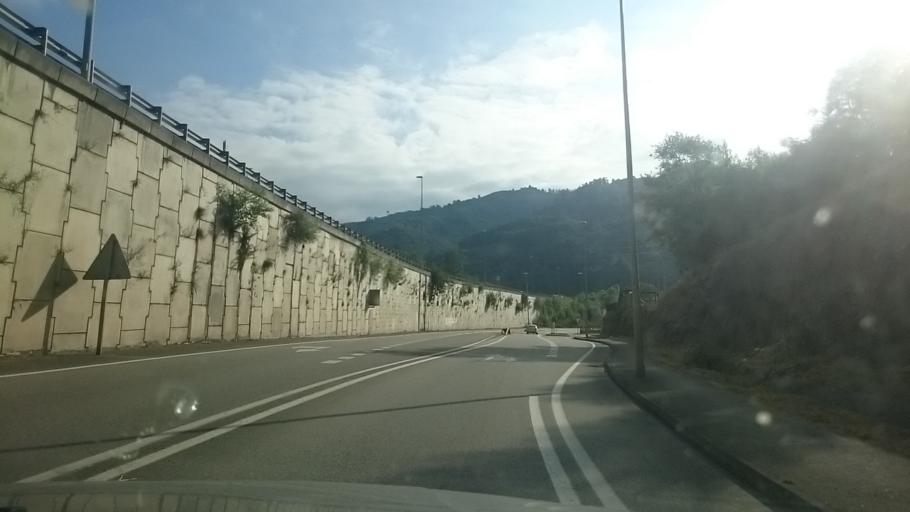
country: ES
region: Asturias
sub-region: Province of Asturias
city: Sama
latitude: 43.3238
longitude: -5.7356
